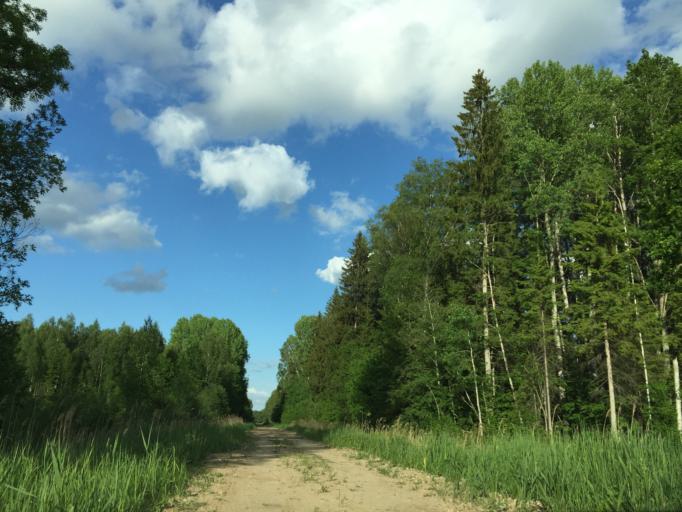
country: LV
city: Tireli
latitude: 56.7778
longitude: 23.4091
